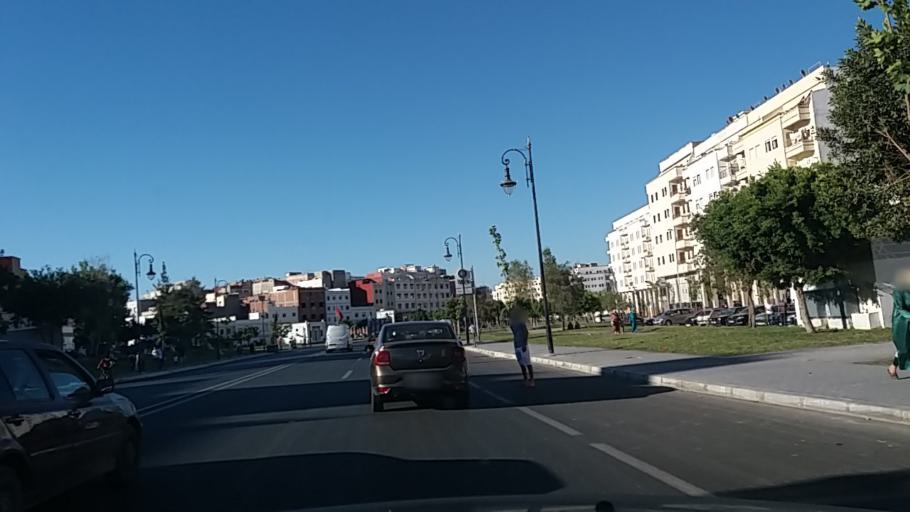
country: MA
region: Tanger-Tetouan
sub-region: Tanger-Assilah
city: Tangier
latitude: 35.7393
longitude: -5.8008
